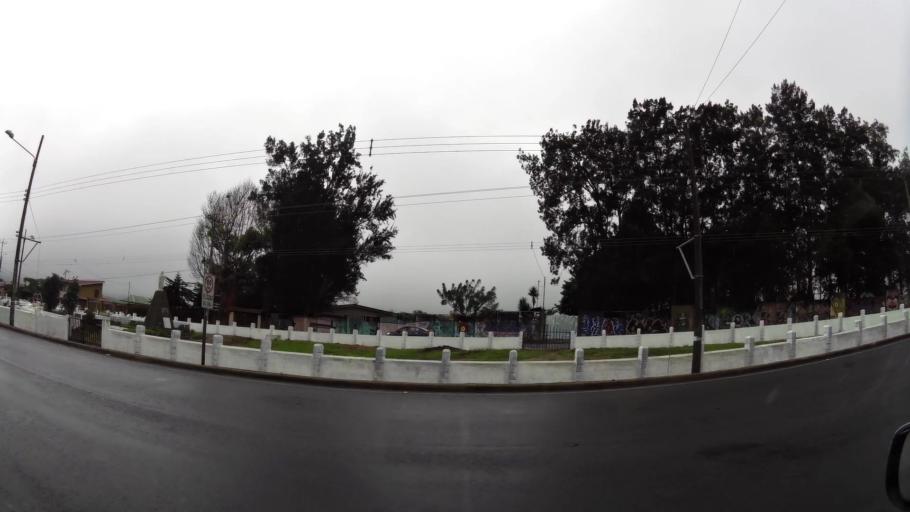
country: CR
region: Cartago
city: Paraiso
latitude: 9.8399
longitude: -83.8757
